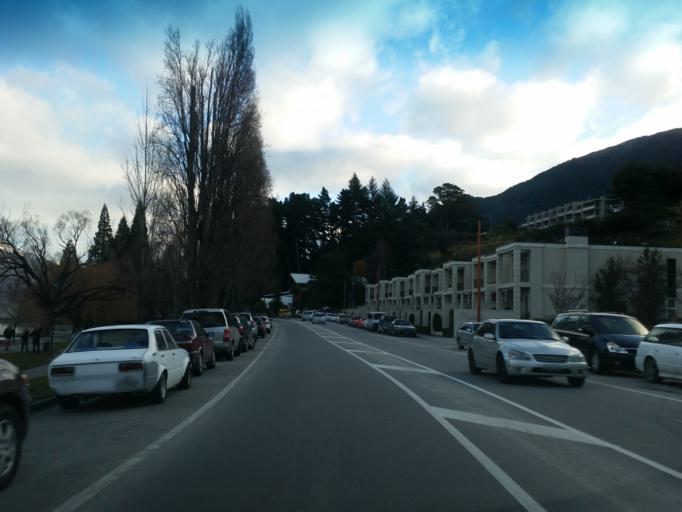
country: NZ
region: Otago
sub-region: Queenstown-Lakes District
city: Queenstown
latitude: -45.0354
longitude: 168.6518
